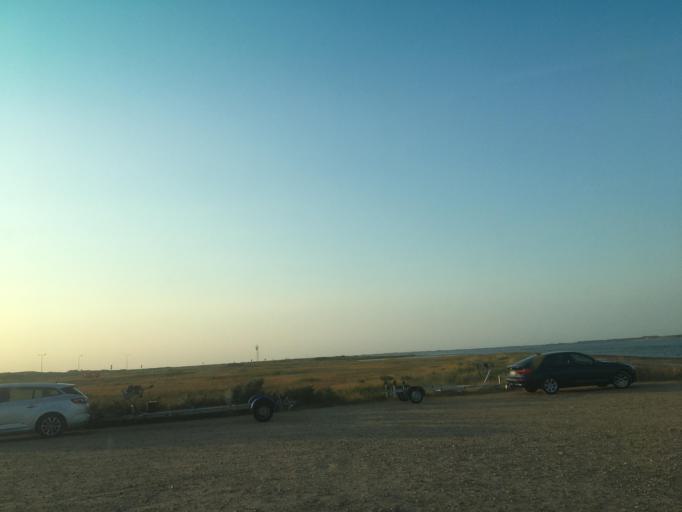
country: DK
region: Central Jutland
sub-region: Lemvig Kommune
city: Thyboron
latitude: 56.7021
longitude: 8.2471
